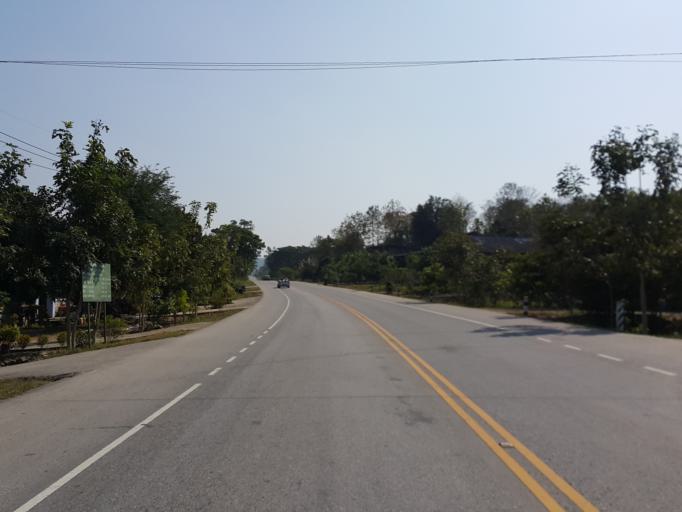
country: TH
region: Lampang
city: Wang Nuea
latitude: 18.9997
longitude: 99.6124
